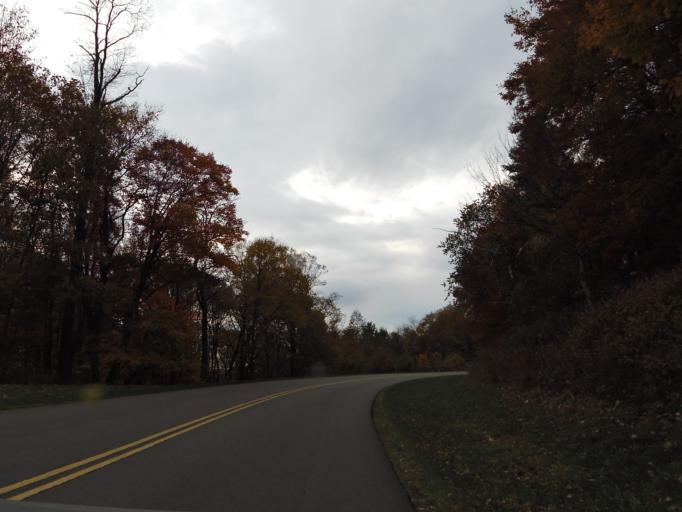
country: US
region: North Carolina
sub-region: Wilkes County
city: Mulberry
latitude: 36.3643
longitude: -81.3055
